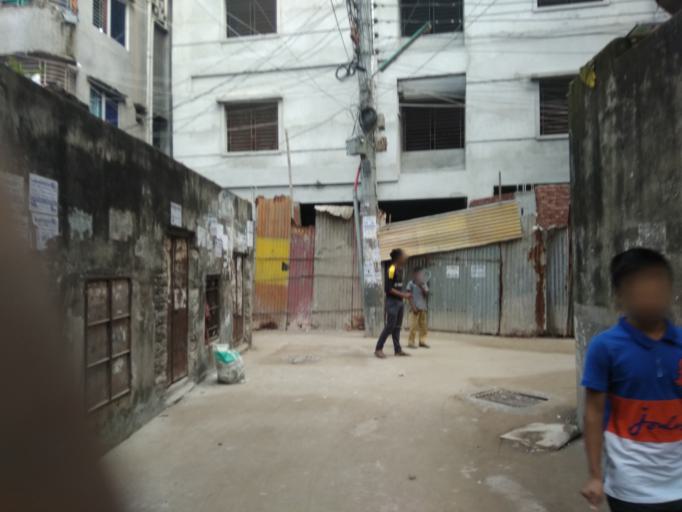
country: BD
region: Dhaka
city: Paltan
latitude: 23.7850
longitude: 90.4235
